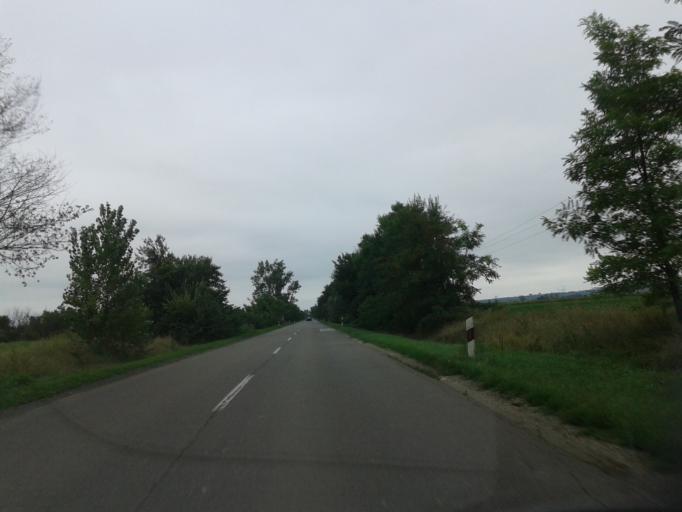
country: HU
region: Bacs-Kiskun
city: Szalkszentmarton
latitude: 46.9841
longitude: 19.0064
